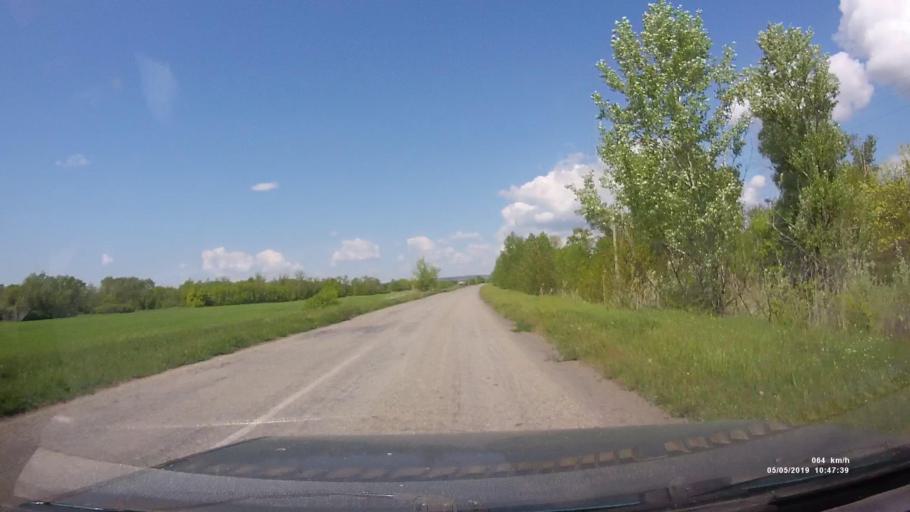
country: RU
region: Rostov
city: Ust'-Donetskiy
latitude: 47.6393
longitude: 40.8298
